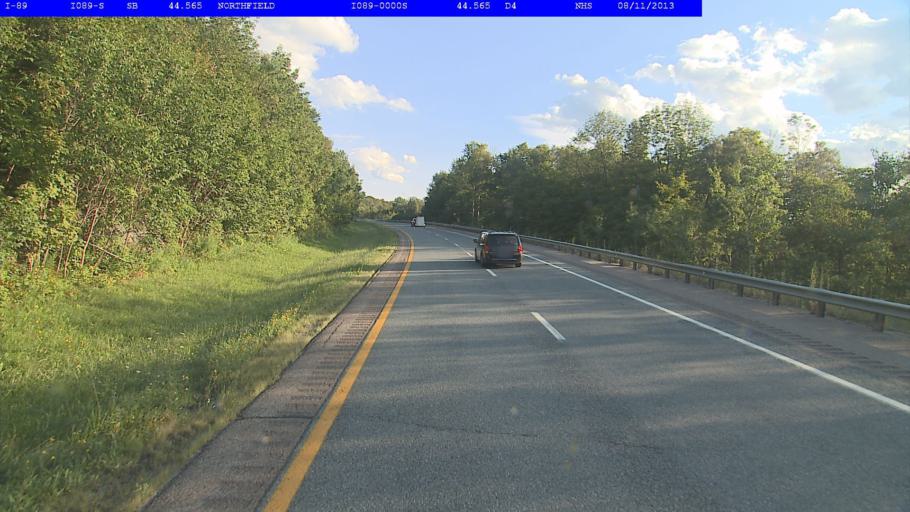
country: US
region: Vermont
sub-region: Washington County
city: Northfield
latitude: 44.1379
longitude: -72.6010
